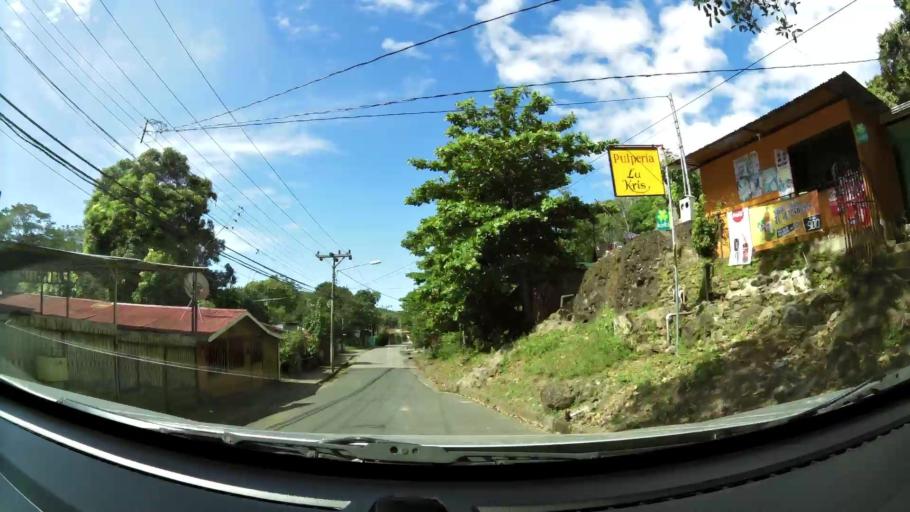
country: CR
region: Guanacaste
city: Juntas
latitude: 10.2822
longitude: -84.9496
